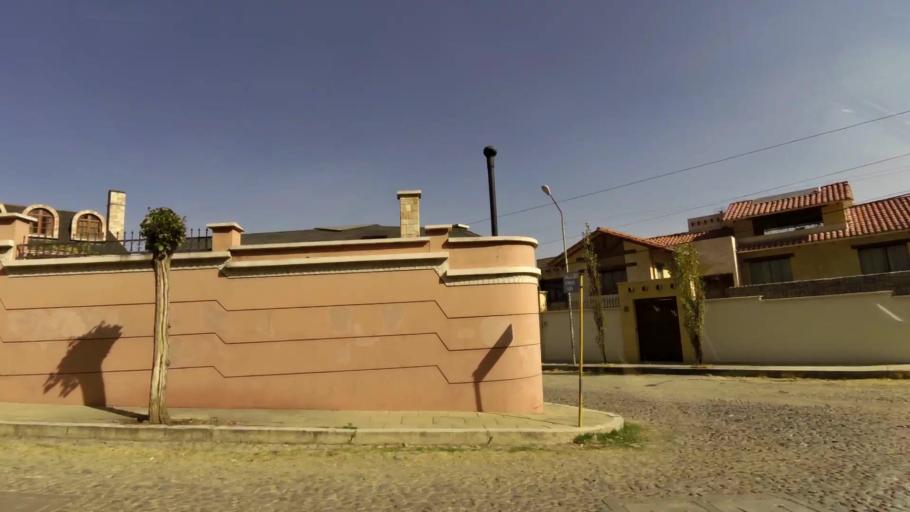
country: BO
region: La Paz
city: La Paz
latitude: -16.5128
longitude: -68.0618
